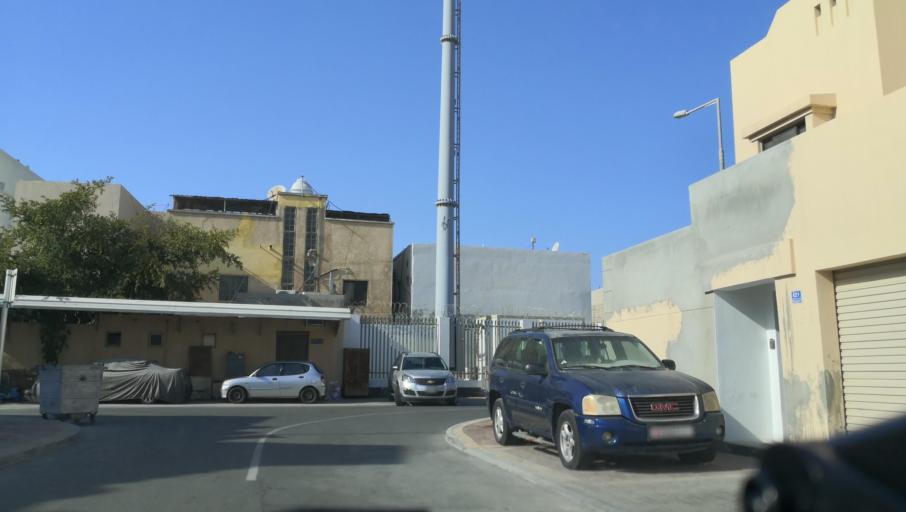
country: BH
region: Muharraq
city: Al Muharraq
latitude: 26.2502
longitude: 50.6310
